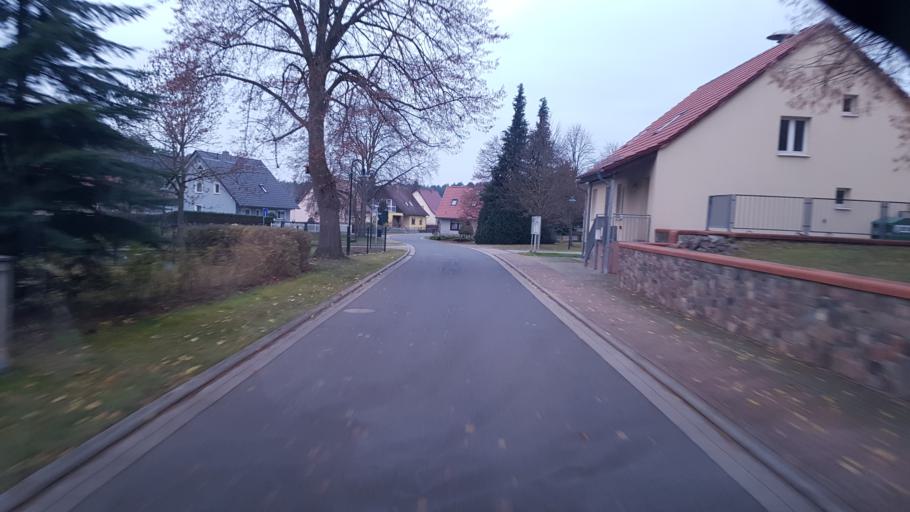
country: DE
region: Brandenburg
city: Gross Lindow
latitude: 52.1106
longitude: 14.4962
